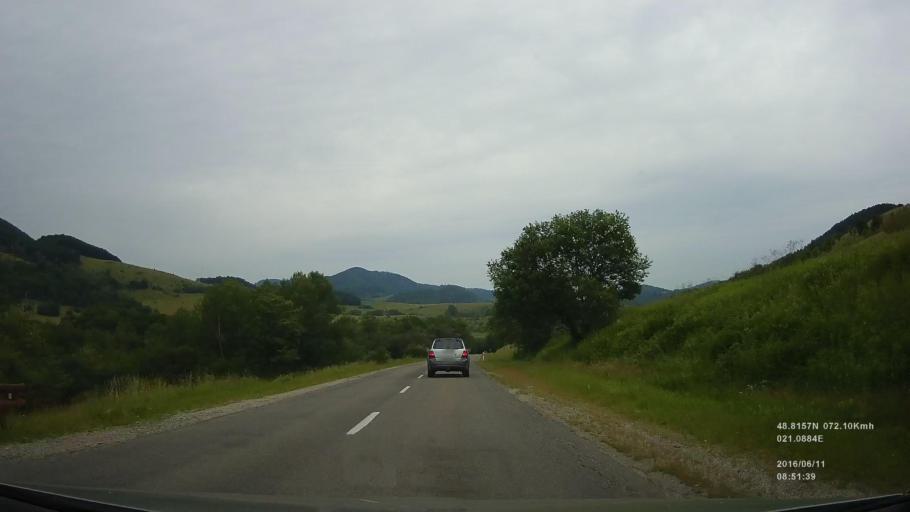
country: SK
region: Kosicky
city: Gelnica
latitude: 48.8110
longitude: 21.0958
